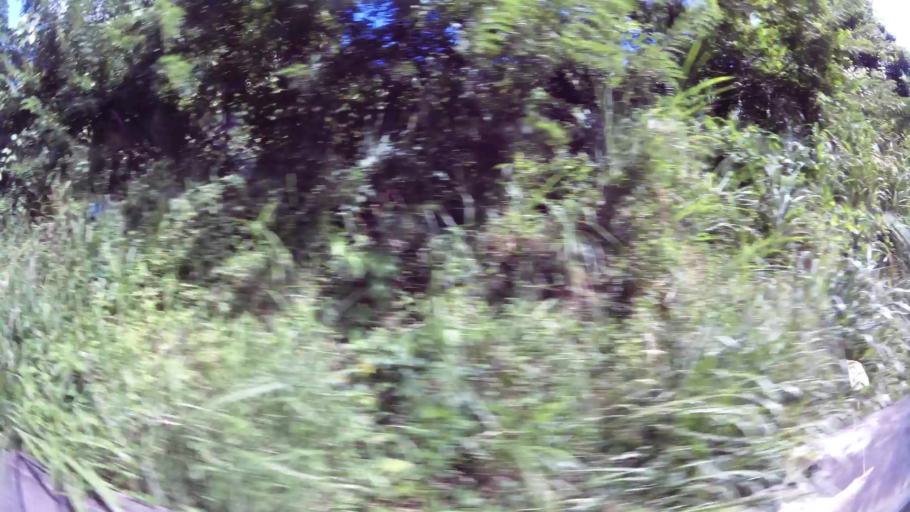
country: DM
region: Saint Luke
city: Pointe Michel
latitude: 15.2827
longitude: -61.3746
